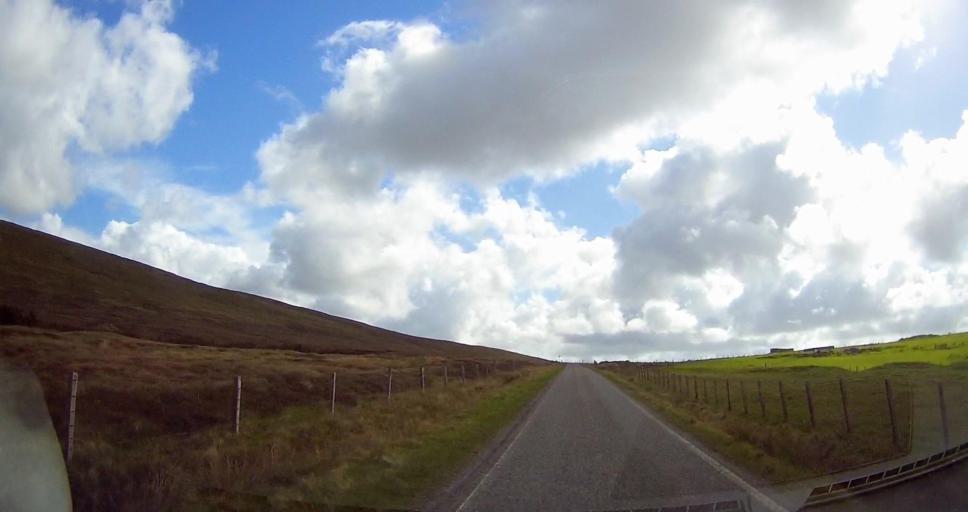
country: GB
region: Scotland
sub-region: Shetland Islands
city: Lerwick
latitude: 60.5098
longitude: -1.3863
